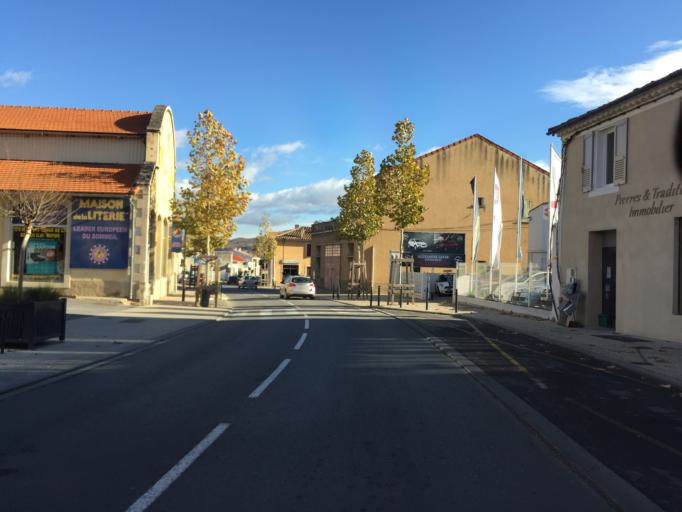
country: FR
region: Provence-Alpes-Cote d'Azur
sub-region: Departement du Vaucluse
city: Apt
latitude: 43.8785
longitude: 5.3866
